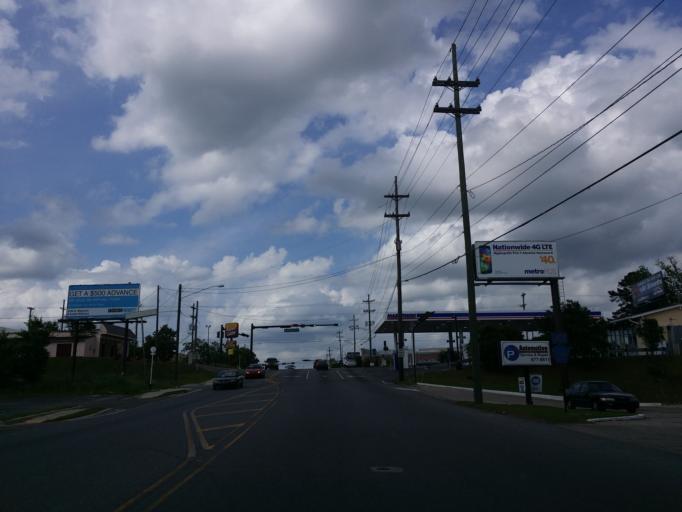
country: US
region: Florida
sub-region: Leon County
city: Tallahassee
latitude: 30.4346
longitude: -84.2618
